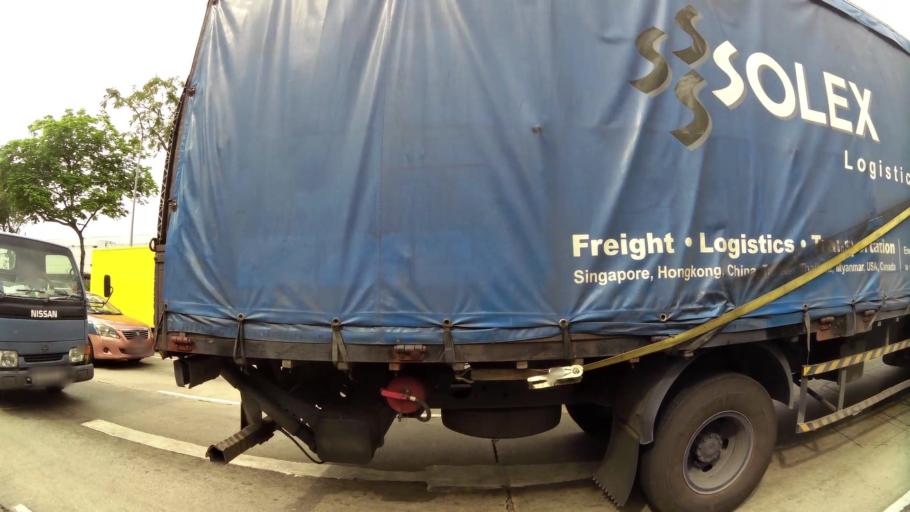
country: MY
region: Johor
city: Johor Bahru
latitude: 1.4458
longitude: 103.8081
